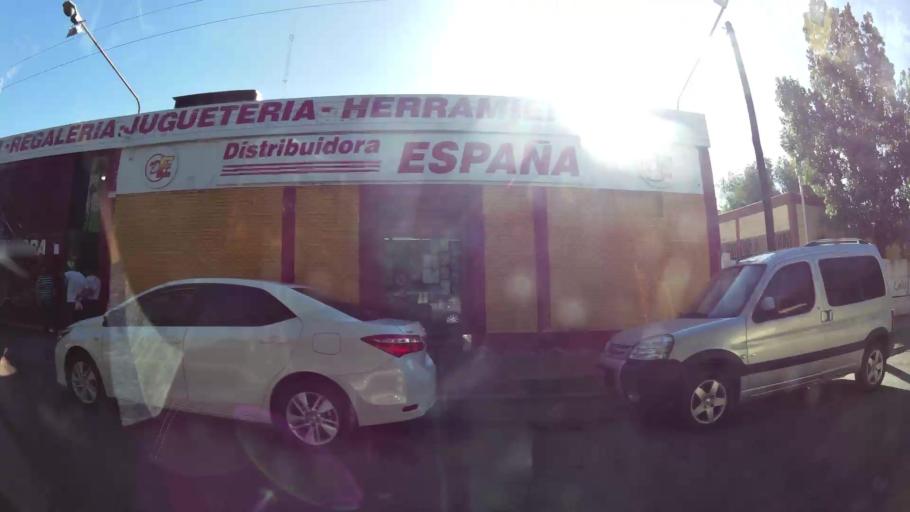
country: AR
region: San Juan
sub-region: Departamento de Santa Lucia
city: Santa Lucia
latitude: -31.5411
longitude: -68.5100
